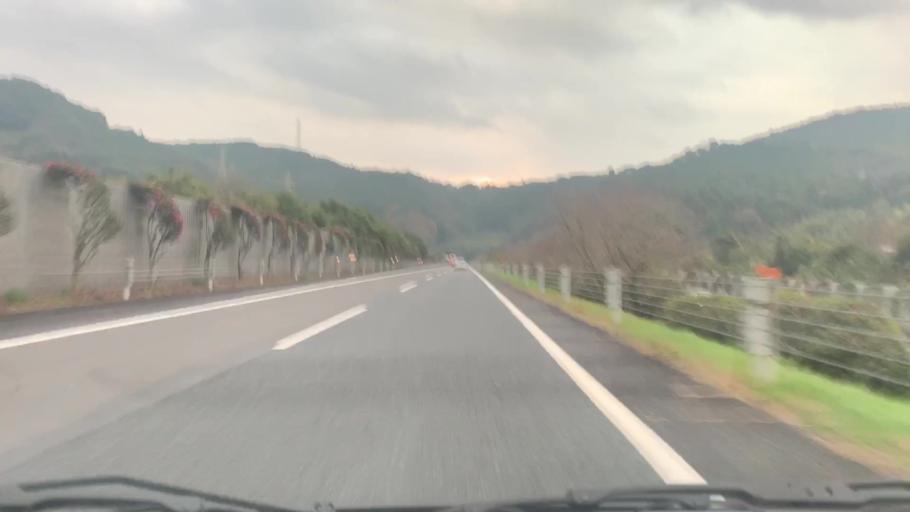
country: JP
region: Nagasaki
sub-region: Isahaya-shi
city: Isahaya
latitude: 32.8790
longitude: 129.9966
